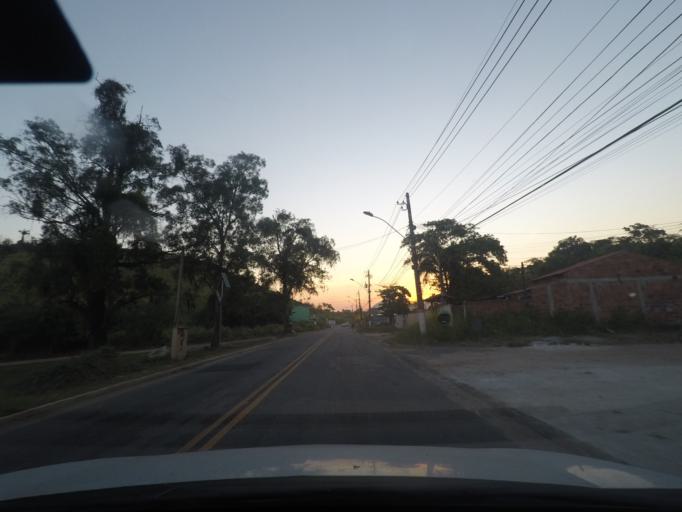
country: BR
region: Rio de Janeiro
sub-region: Marica
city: Marica
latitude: -22.9463
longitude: -42.9646
